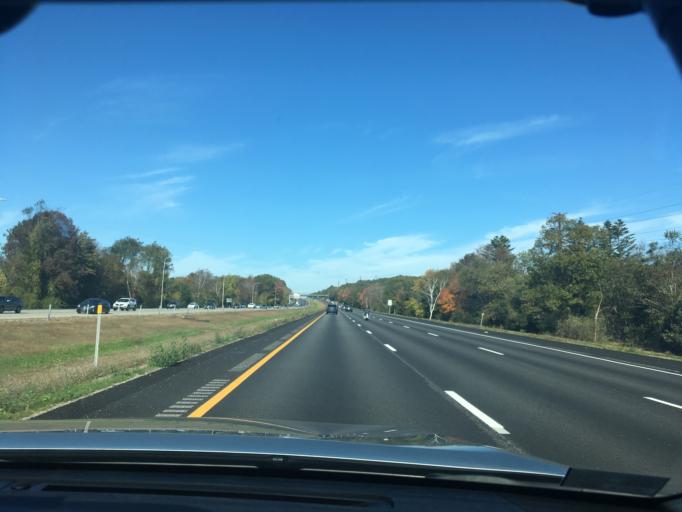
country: US
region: Rhode Island
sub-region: Kent County
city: East Greenwich
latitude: 41.6377
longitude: -71.4871
